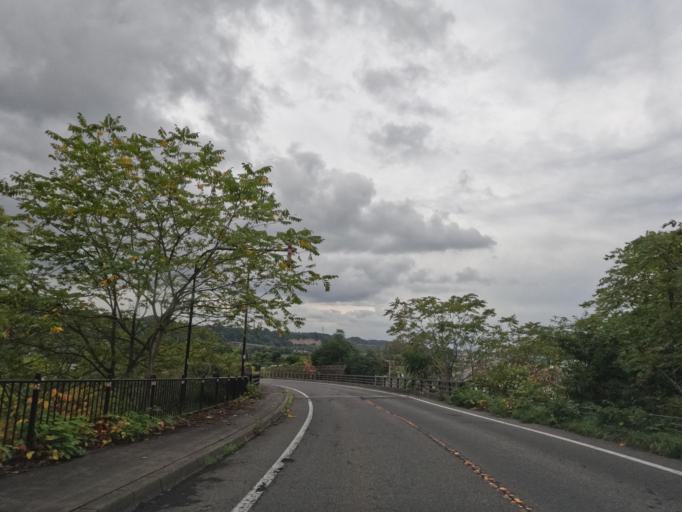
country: JP
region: Hokkaido
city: Date
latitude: 42.5221
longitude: 140.8609
